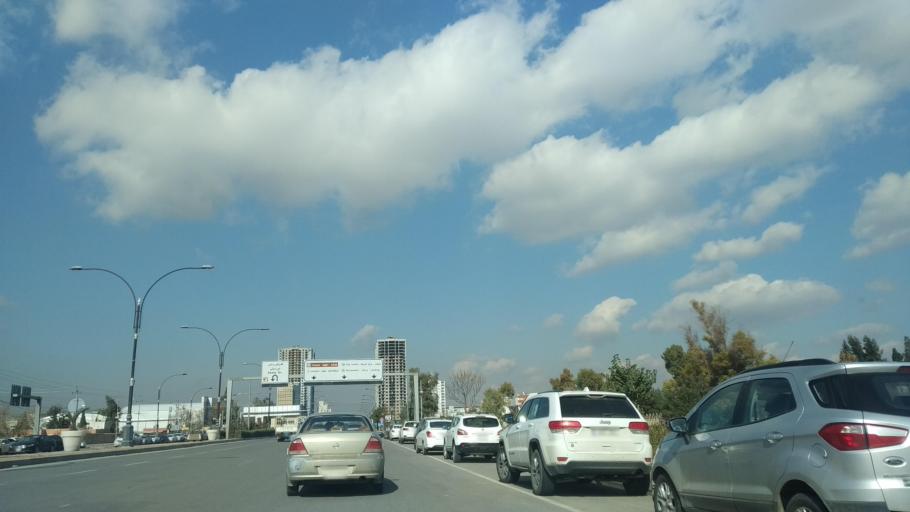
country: IQ
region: Arbil
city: Erbil
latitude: 36.1404
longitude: 44.0209
